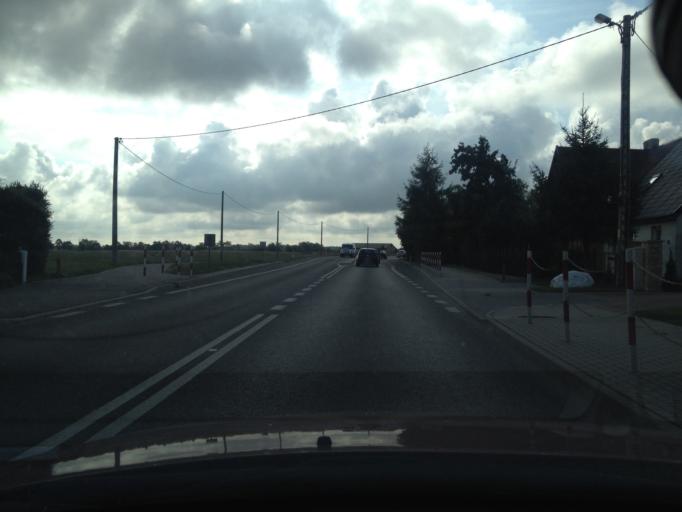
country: PL
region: West Pomeranian Voivodeship
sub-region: Powiat kamienski
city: Dziwnow
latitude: 54.0126
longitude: 14.8145
